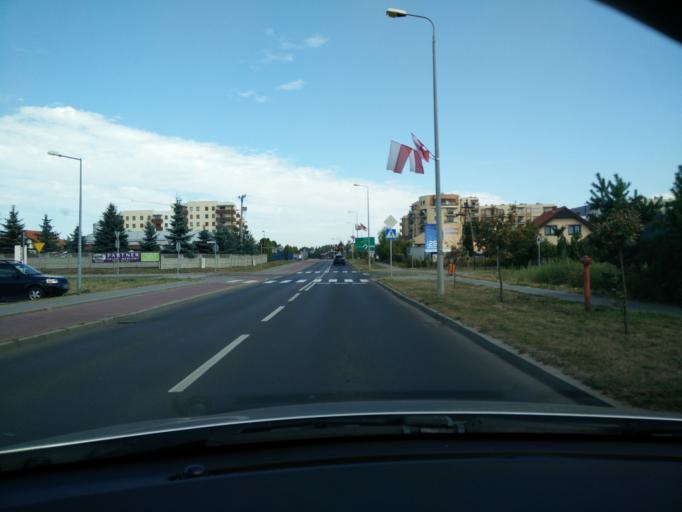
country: PL
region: Greater Poland Voivodeship
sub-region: Powiat sredzki
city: Sroda Wielkopolska
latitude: 52.2342
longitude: 17.2685
